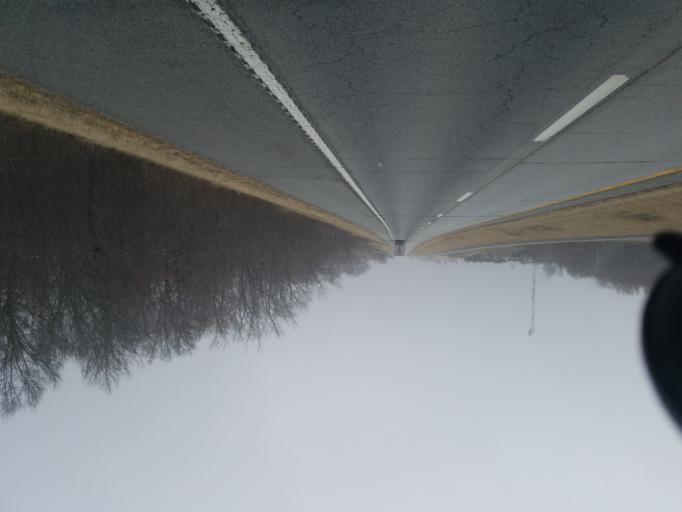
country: US
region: Missouri
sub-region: Macon County
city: La Plata
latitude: 39.9240
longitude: -92.4755
